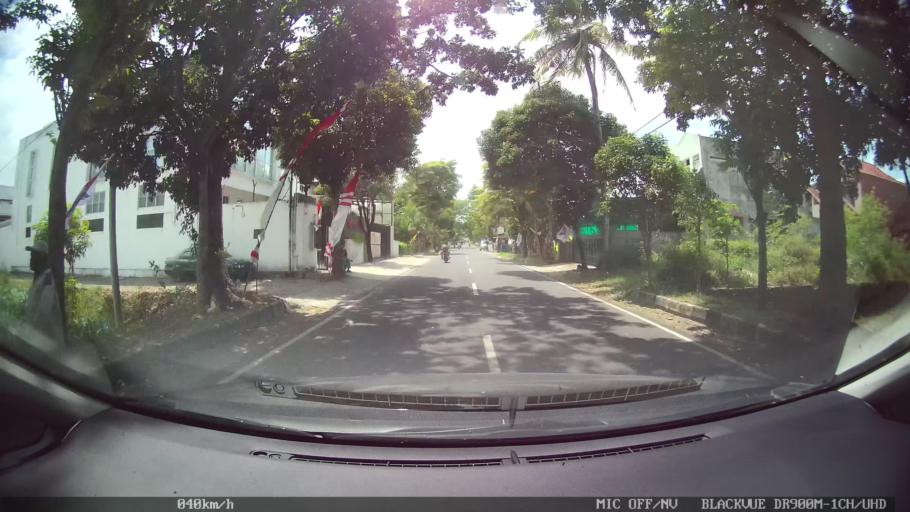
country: ID
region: Daerah Istimewa Yogyakarta
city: Bantul
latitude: -7.8839
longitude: 110.3356
